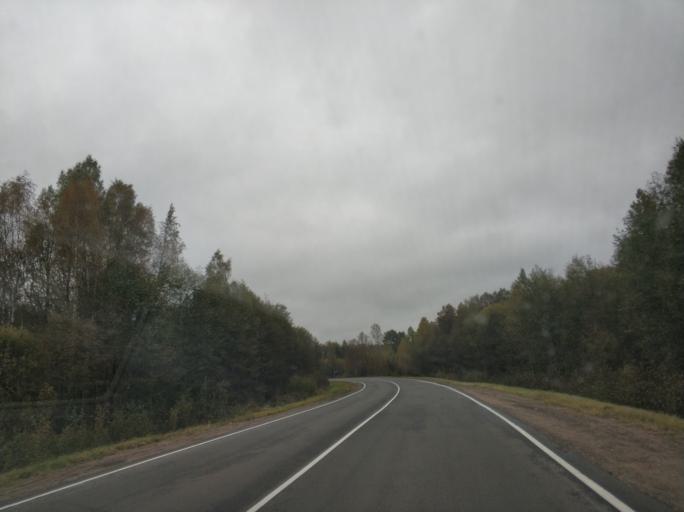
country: BY
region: Vitebsk
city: Rasony
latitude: 56.1002
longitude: 28.7245
